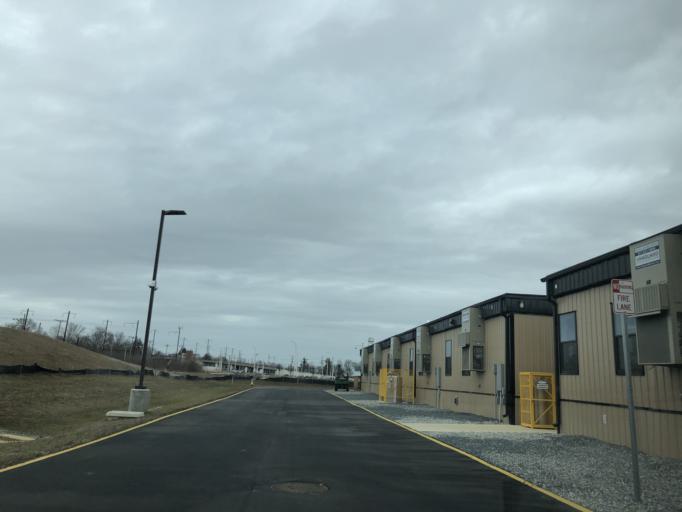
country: US
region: Delaware
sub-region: New Castle County
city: Newark
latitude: 39.6673
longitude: -75.7575
